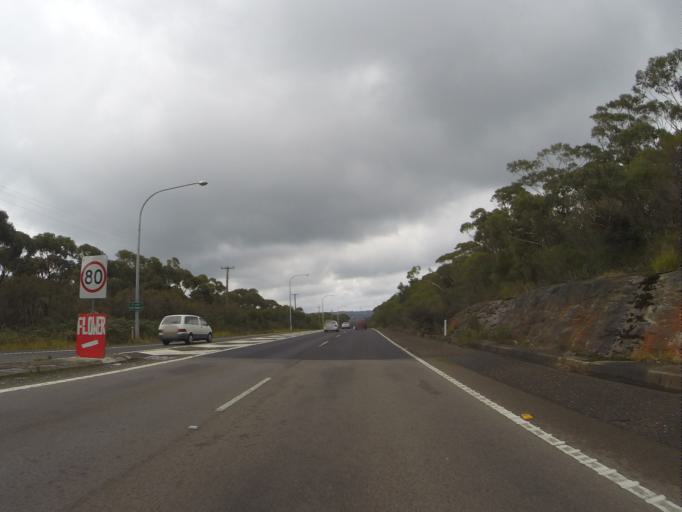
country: AU
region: New South Wales
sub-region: Wollongong
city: Bulli
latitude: -34.2991
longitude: 150.9145
